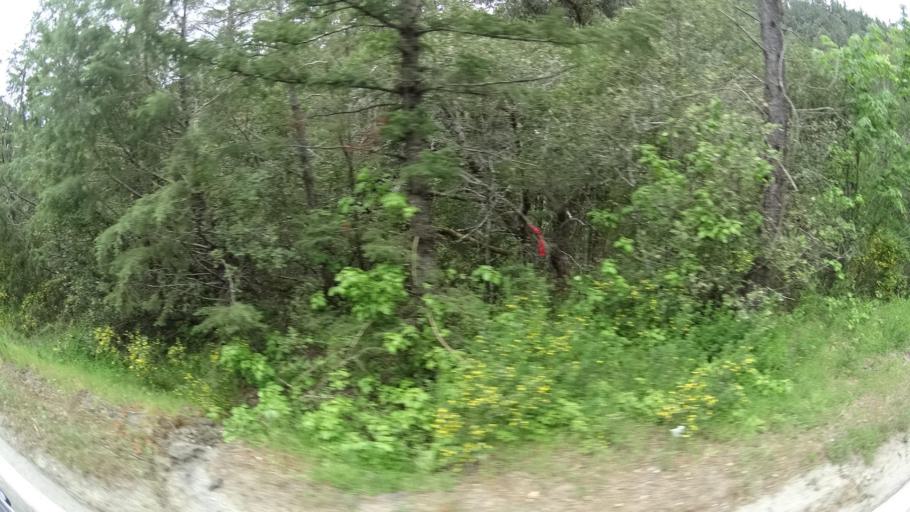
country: US
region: California
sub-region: Humboldt County
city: Redway
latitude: 40.1276
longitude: -123.8670
